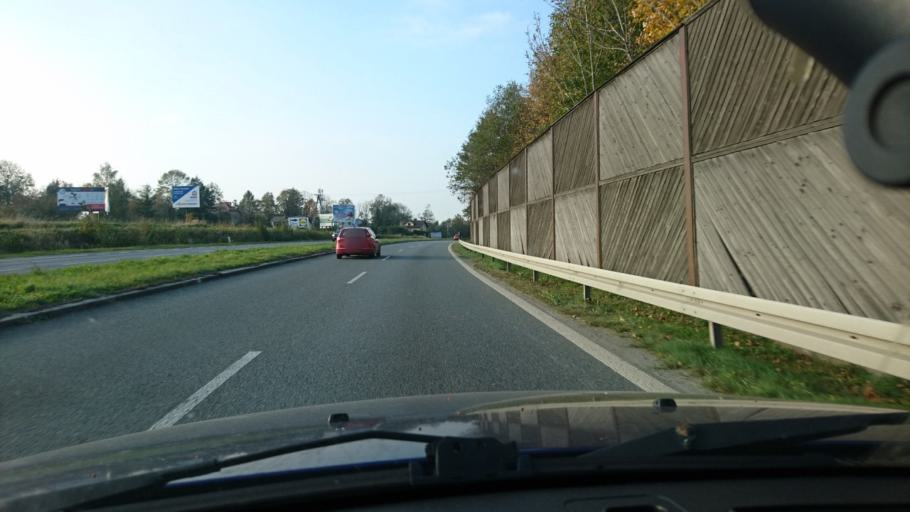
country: PL
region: Silesian Voivodeship
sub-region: Powiat cieszynski
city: Ustron
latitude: 49.7190
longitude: 18.7979
